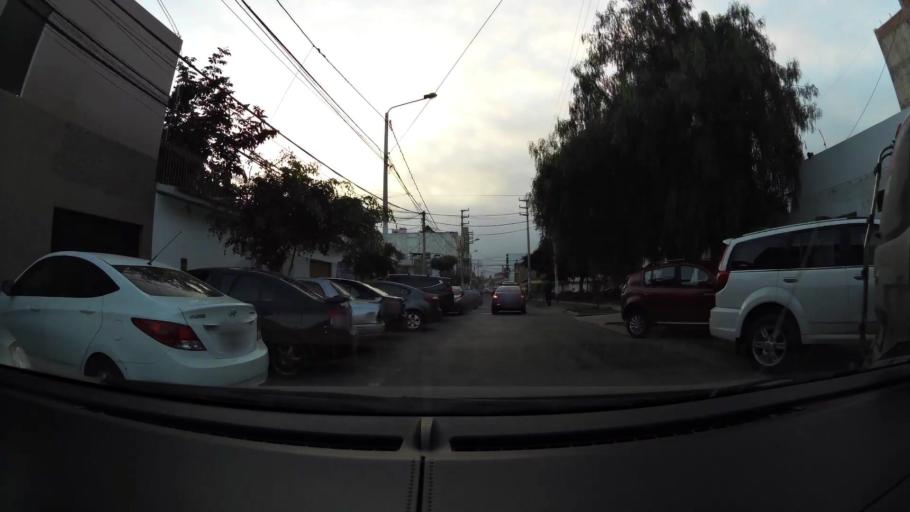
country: PE
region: La Libertad
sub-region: Provincia de Trujillo
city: Trujillo
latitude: -8.1030
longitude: -79.0374
